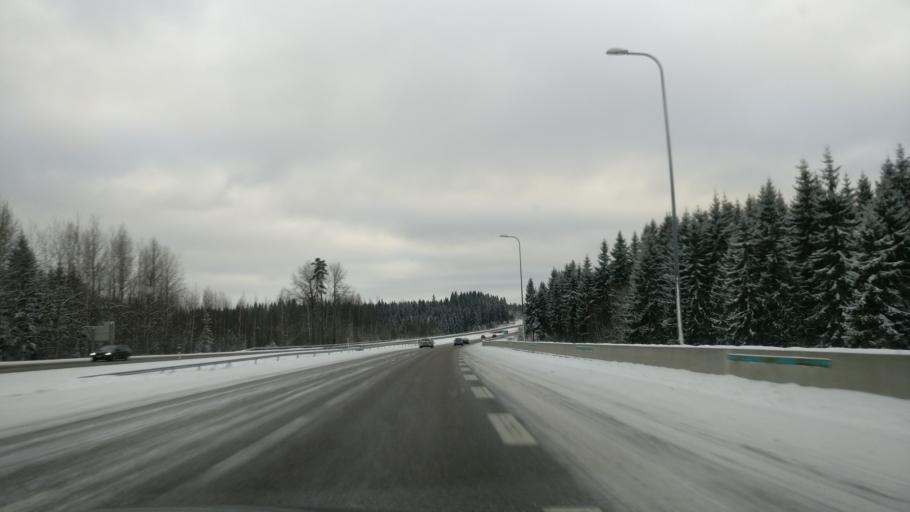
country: FI
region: Paijanne Tavastia
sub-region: Lahti
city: Nastola
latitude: 61.0425
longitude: 25.8516
